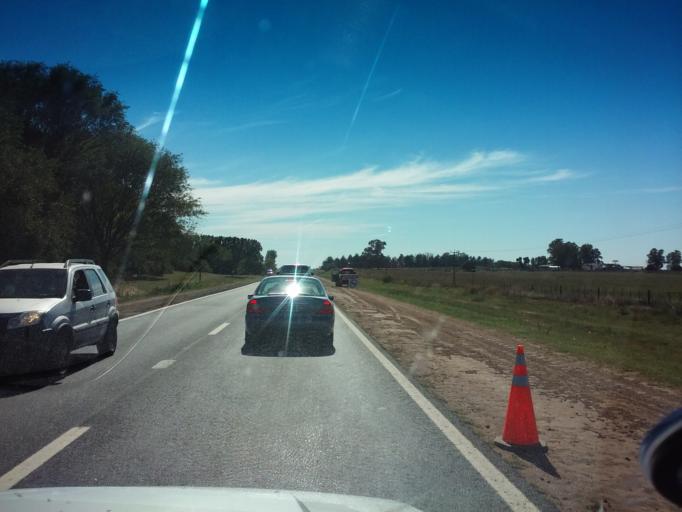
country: AR
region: Buenos Aires
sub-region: Partido de Nueve de Julio
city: Nueve de Julio
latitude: -35.4587
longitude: -60.8337
